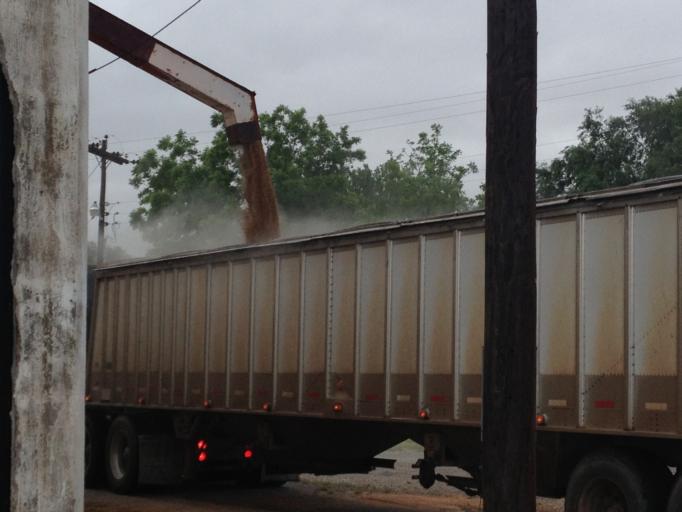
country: US
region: Oklahoma
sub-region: Alfalfa County
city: Helena
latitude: 36.6645
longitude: -98.0517
